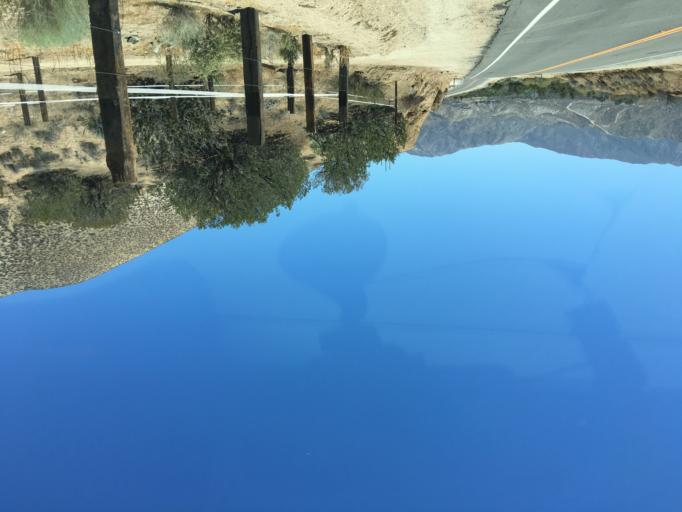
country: US
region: California
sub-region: Los Angeles County
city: Acton
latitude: 34.4527
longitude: -118.2024
